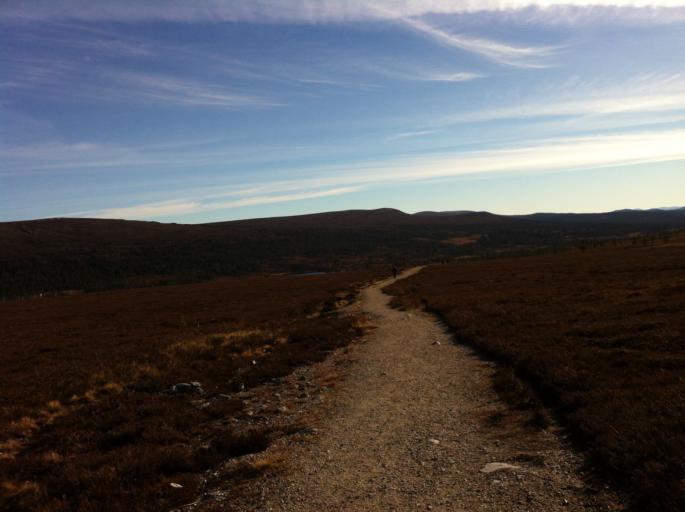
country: NO
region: Hedmark
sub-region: Engerdal
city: Engerdal
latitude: 62.1147
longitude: 12.2674
